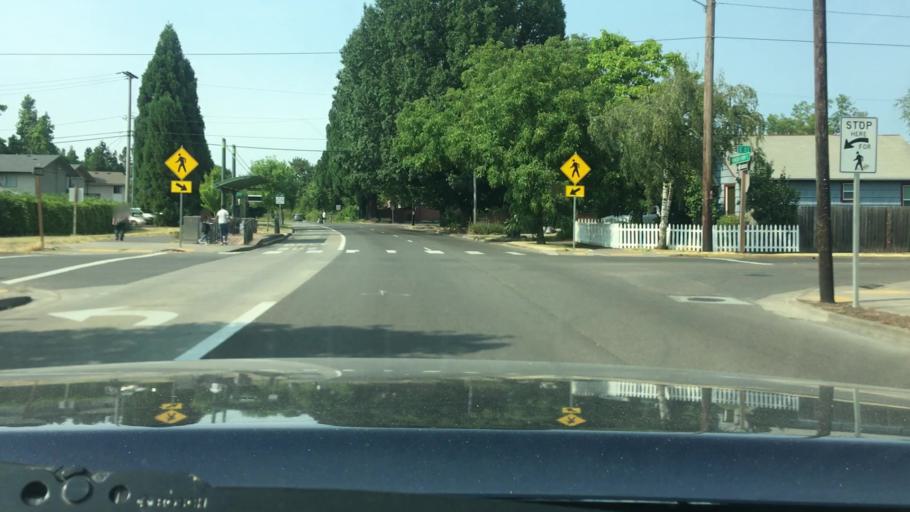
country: US
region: Oregon
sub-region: Lane County
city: Springfield
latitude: 44.0504
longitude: -123.0220
